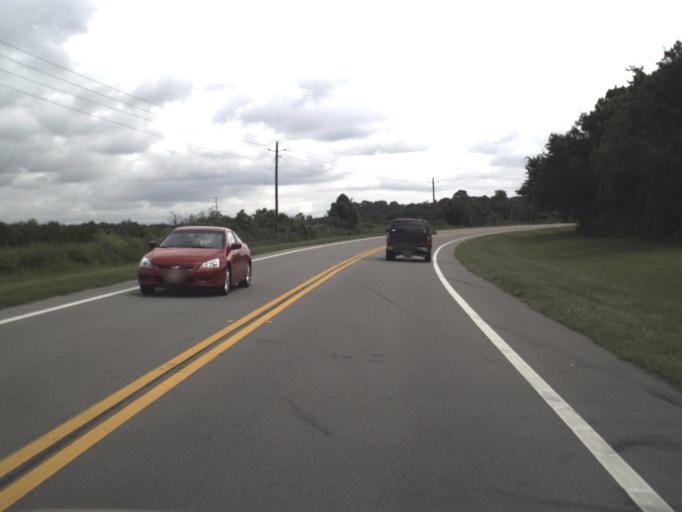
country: US
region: Florida
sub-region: Hillsborough County
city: Wimauma
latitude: 27.6021
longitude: -82.3197
